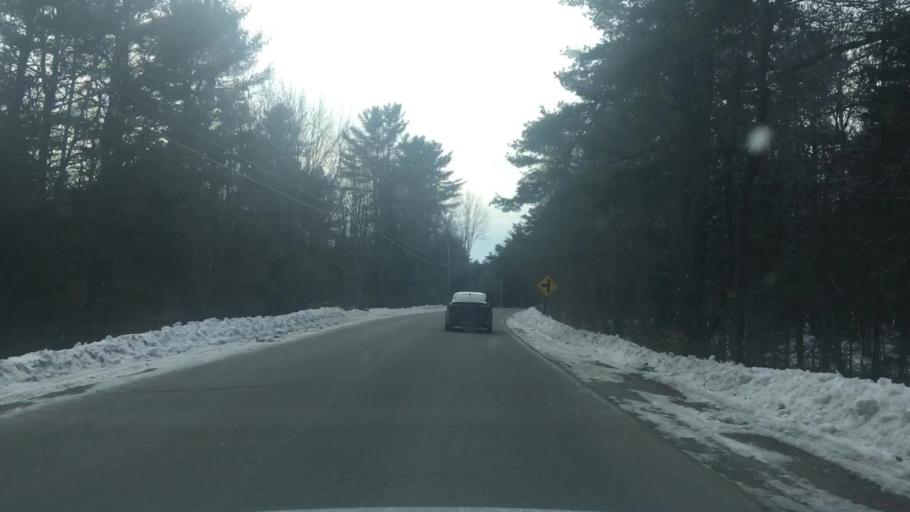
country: US
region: Maine
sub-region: Hancock County
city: Orland
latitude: 44.6261
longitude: -68.6992
